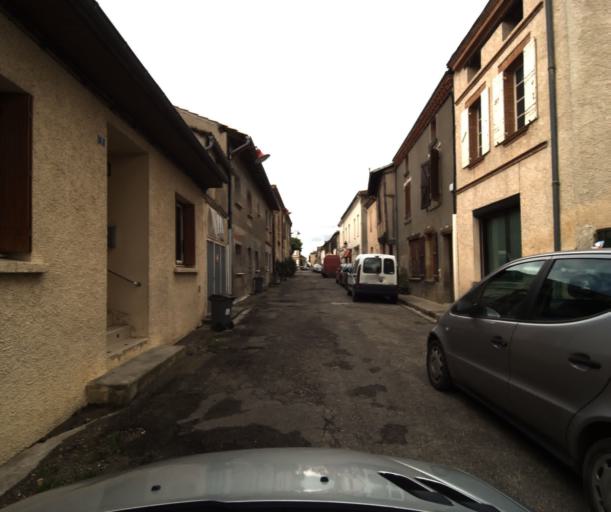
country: FR
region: Midi-Pyrenees
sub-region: Departement du Tarn-et-Garonne
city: Lavit
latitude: 43.9583
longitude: 0.9205
